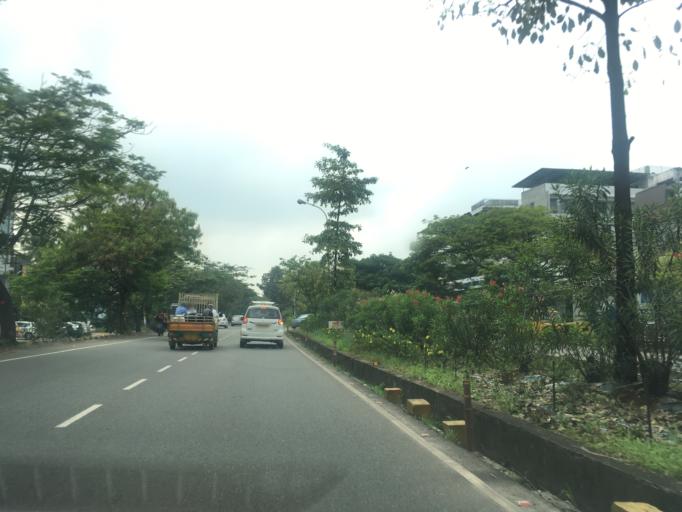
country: IN
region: Kerala
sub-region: Ernakulam
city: Elur
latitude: 10.0197
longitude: 76.3107
